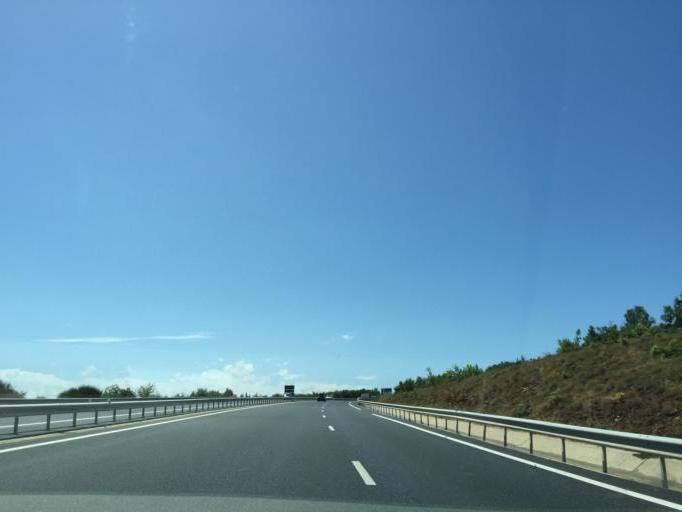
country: FR
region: Midi-Pyrenees
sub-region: Departement de l'Aveyron
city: Millau
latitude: 44.1881
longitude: 3.0555
